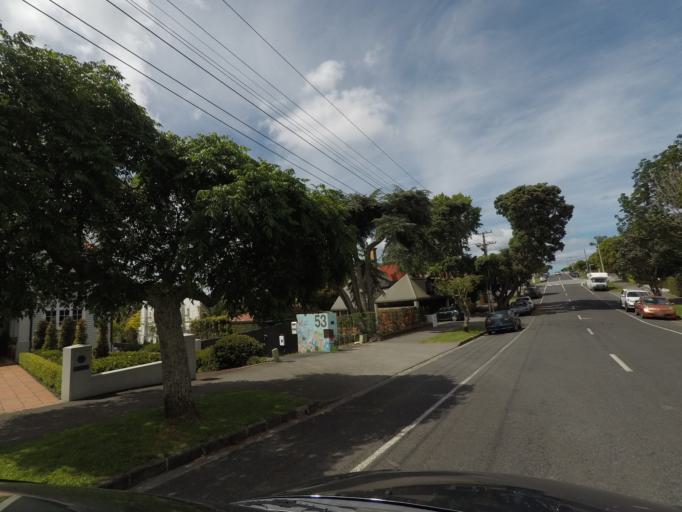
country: NZ
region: Auckland
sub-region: Auckland
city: Auckland
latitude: -36.8444
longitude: 174.7294
